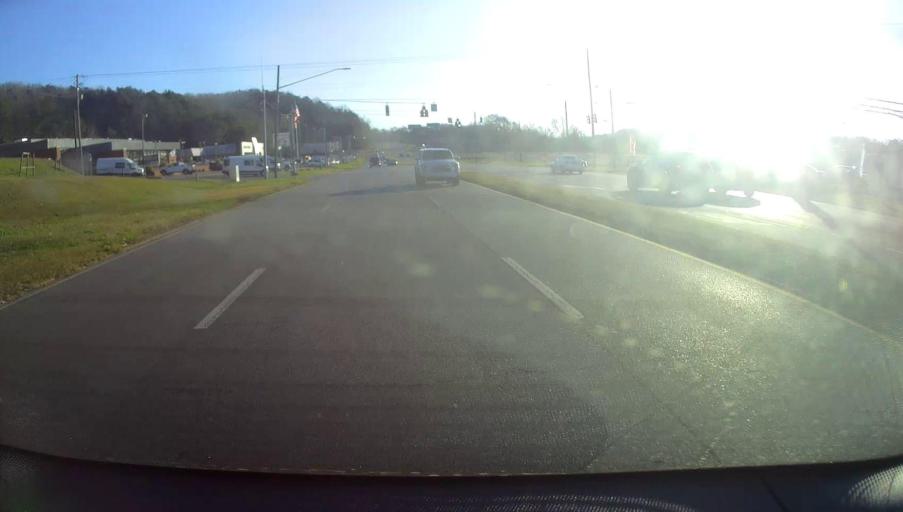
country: US
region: Alabama
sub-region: Calhoun County
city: Oxford
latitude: 33.6299
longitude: -85.8263
